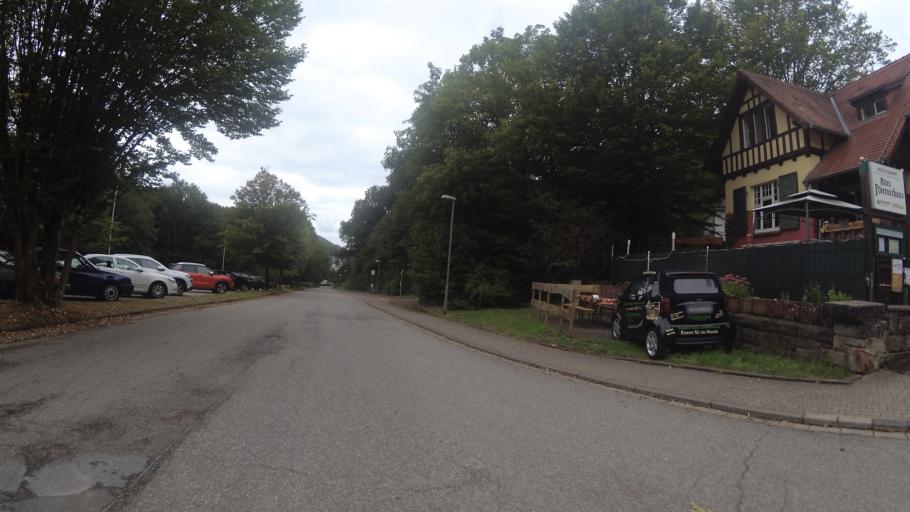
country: DE
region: Saarland
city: Quierschied
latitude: 49.3110
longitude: 7.0365
